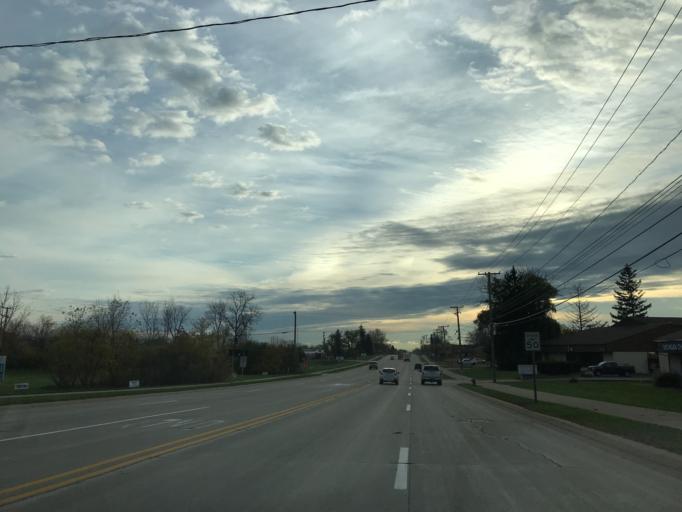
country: US
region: Michigan
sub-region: Oakland County
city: Novi
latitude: 42.4852
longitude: -83.4954
